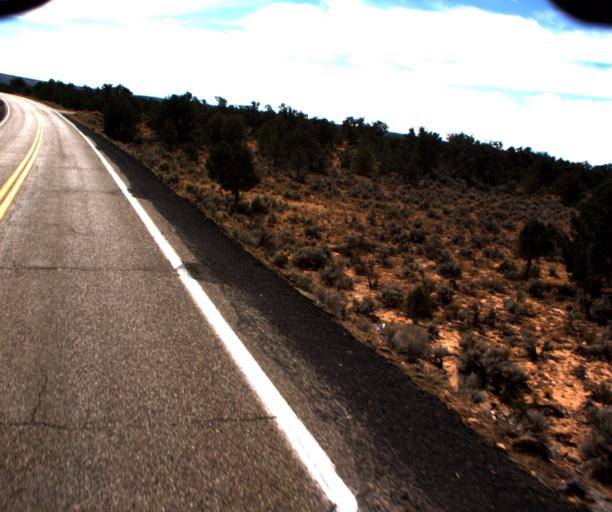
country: US
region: Arizona
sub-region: Navajo County
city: Kayenta
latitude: 36.5914
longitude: -110.4958
